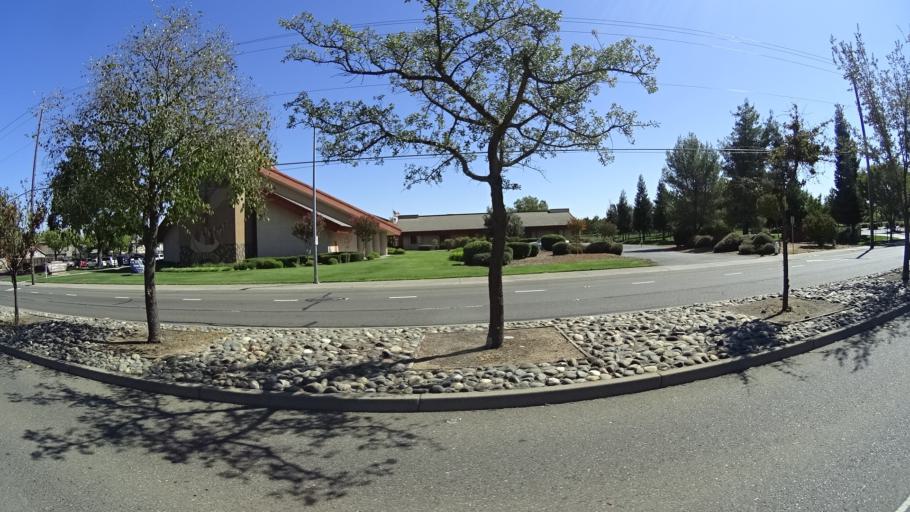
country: US
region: California
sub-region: Sacramento County
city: Elk Grove
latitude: 38.4410
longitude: -121.3717
